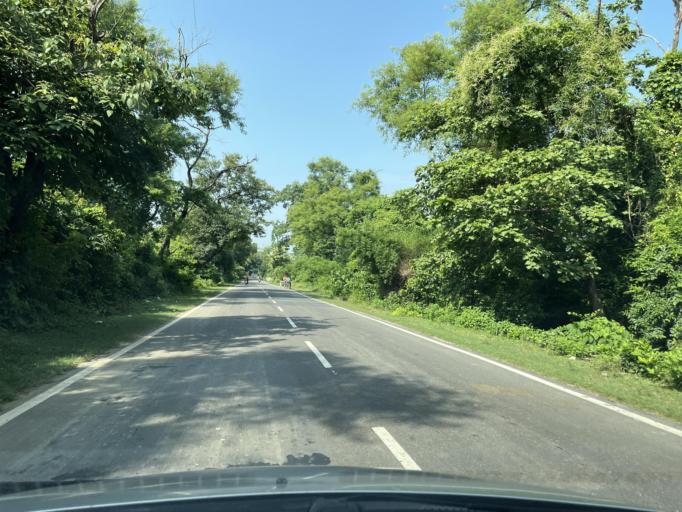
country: IN
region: Uttarakhand
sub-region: Naini Tal
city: Kaladhungi
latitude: 29.2212
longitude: 79.2358
